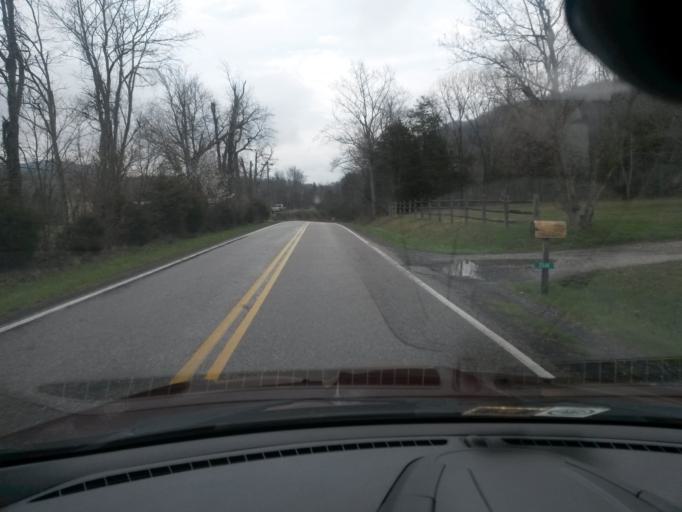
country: US
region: Virginia
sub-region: Bath County
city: Warm Springs
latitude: 37.9235
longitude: -79.7241
